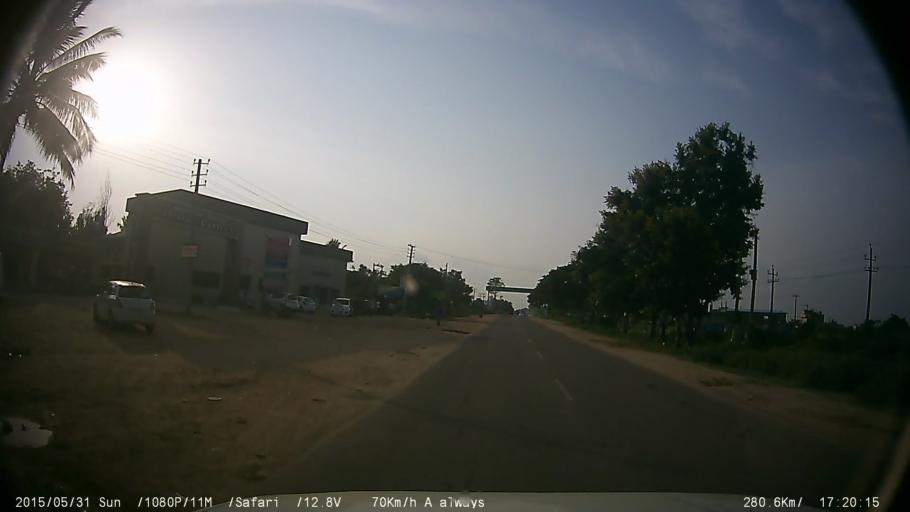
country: IN
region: Karnataka
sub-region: Chamrajnagar
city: Gundlupet
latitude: 11.8217
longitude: 76.6820
